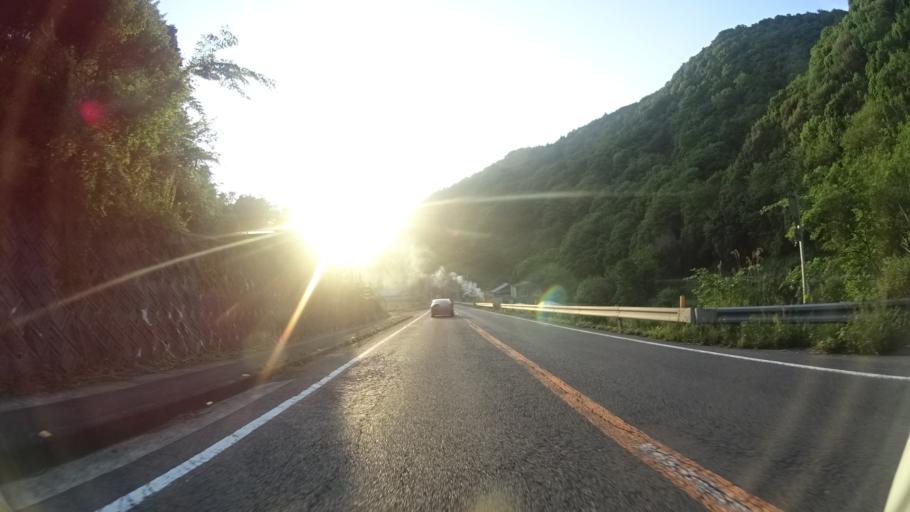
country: JP
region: Ehime
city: Kawanoecho
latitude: 33.9963
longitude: 133.6624
